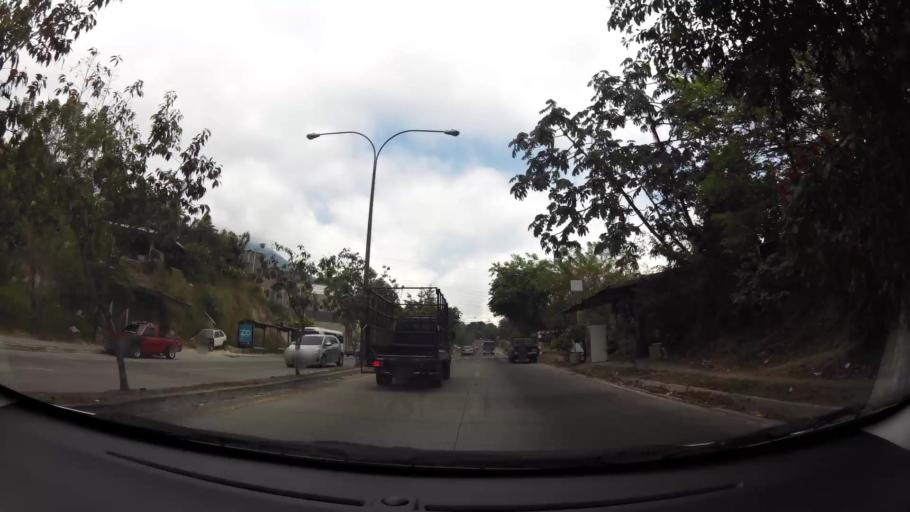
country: SV
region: San Salvador
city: Mejicanos
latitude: 13.7191
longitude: -89.2319
